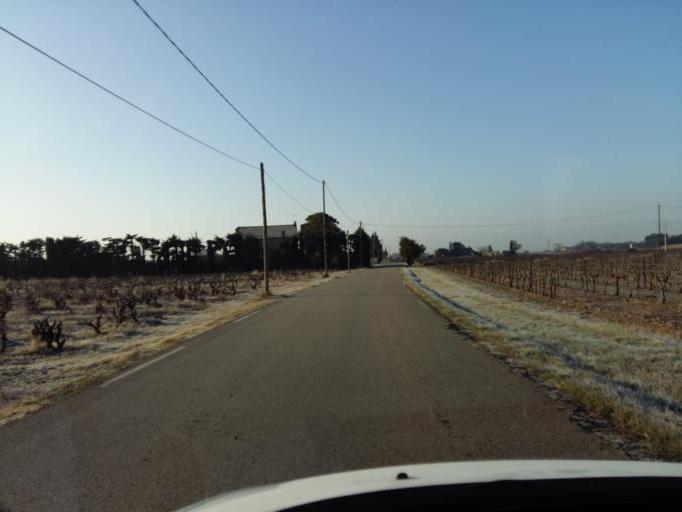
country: FR
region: Provence-Alpes-Cote d'Azur
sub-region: Departement du Vaucluse
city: Sablet
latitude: 44.1988
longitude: 4.9810
